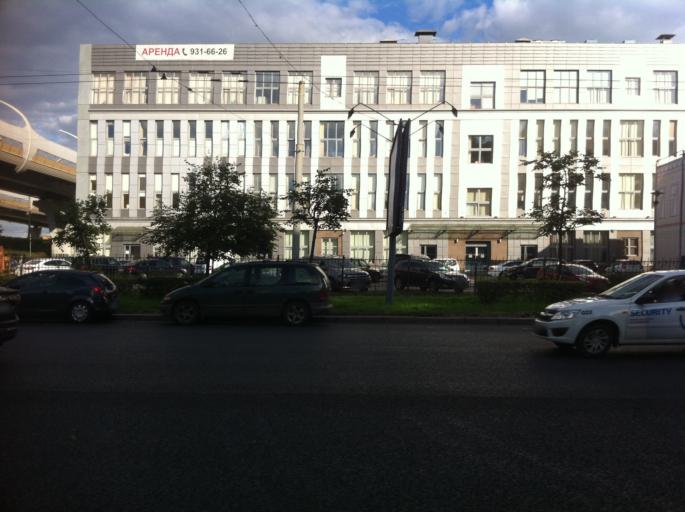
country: RU
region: St.-Petersburg
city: Avtovo
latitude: 59.8841
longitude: 30.2653
